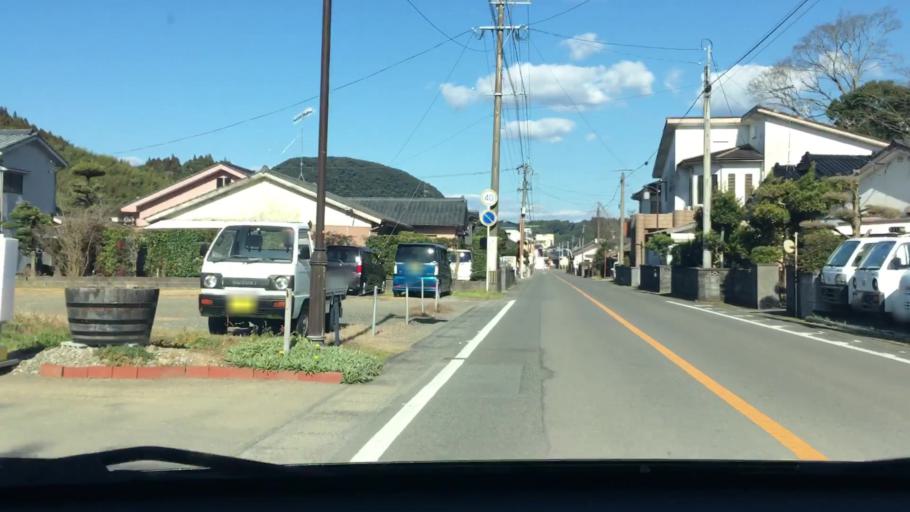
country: JP
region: Kagoshima
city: Satsumasendai
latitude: 31.7859
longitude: 130.4028
